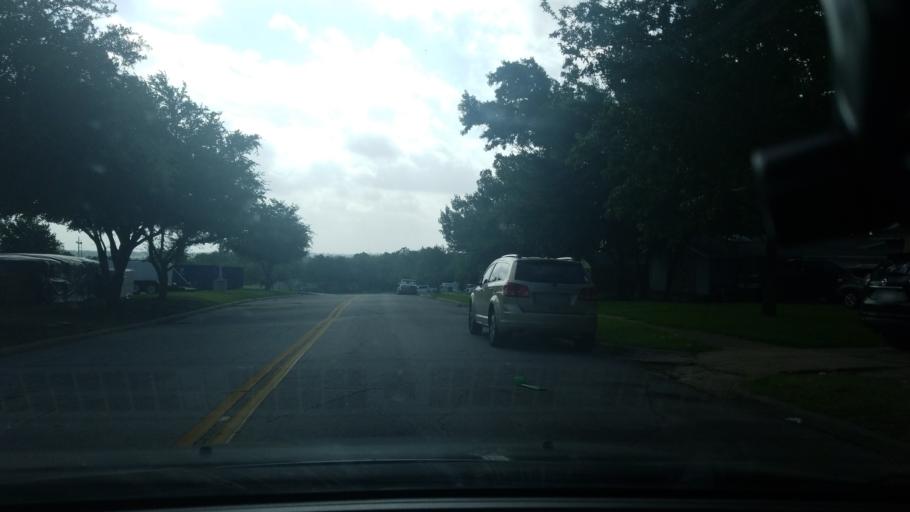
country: US
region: Texas
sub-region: Dallas County
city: Mesquite
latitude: 32.7699
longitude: -96.6349
